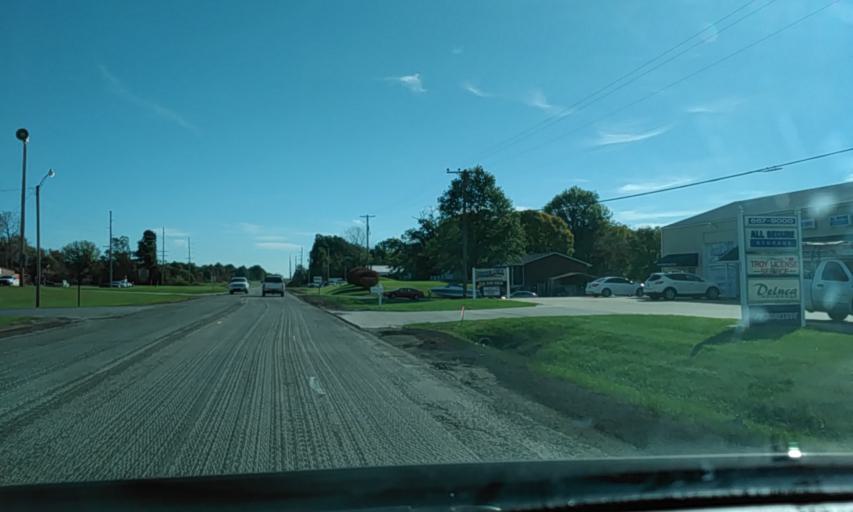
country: US
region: Illinois
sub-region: Madison County
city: Troy
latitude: 38.7177
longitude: -89.8791
